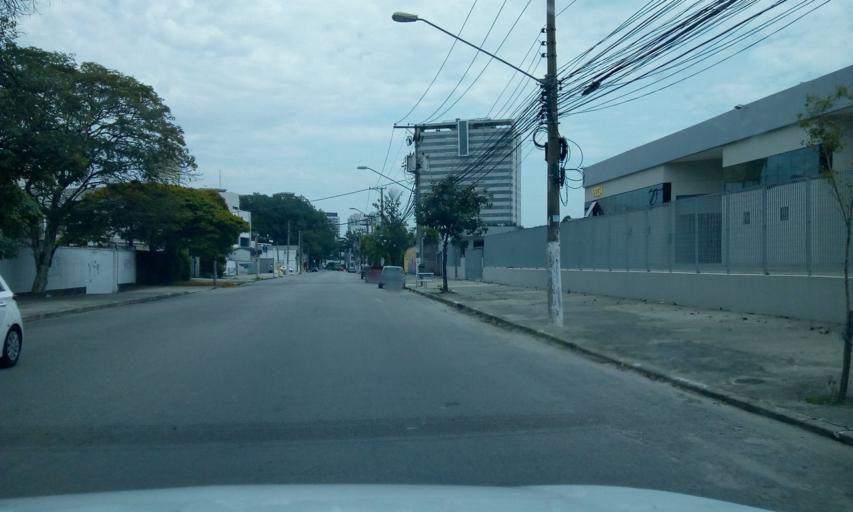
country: BR
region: Sao Paulo
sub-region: Sao Paulo
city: Sao Paulo
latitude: -23.5133
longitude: -46.7065
